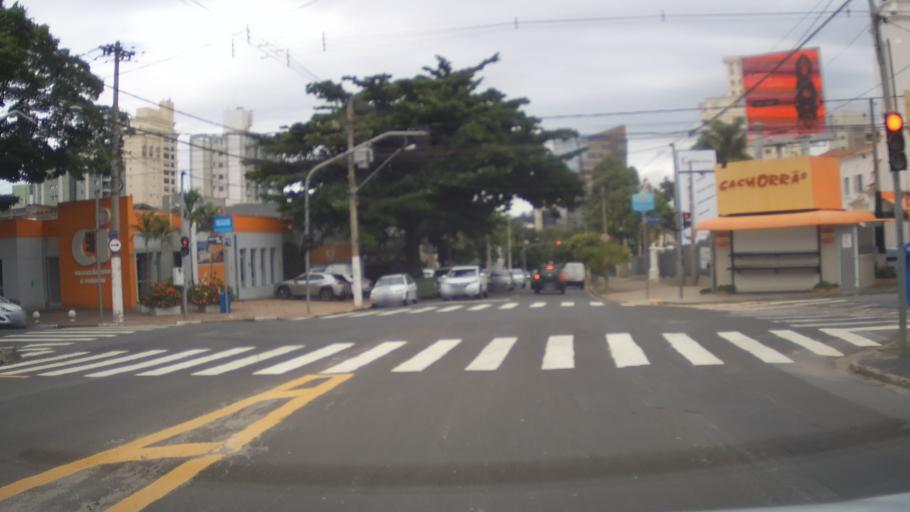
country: BR
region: Sao Paulo
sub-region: Campinas
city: Campinas
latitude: -22.8935
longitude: -47.0515
